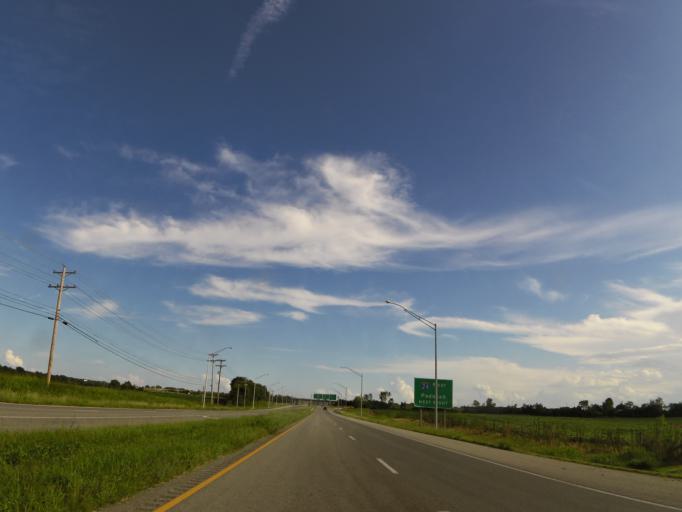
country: US
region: Kentucky
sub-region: Christian County
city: Oak Grove
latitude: 36.7093
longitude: -87.4570
